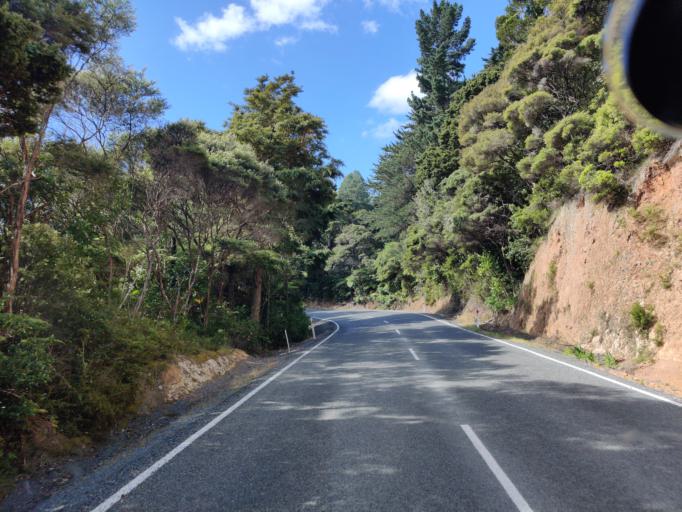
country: NZ
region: Northland
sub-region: Whangarei
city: Ngunguru
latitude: -35.6082
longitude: 174.5236
